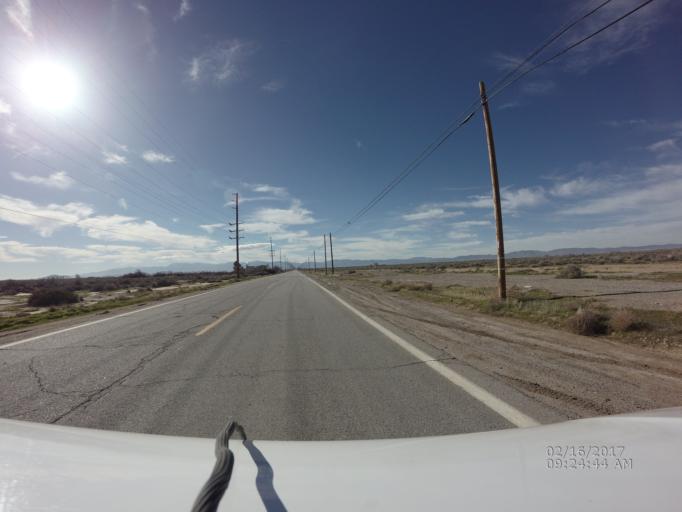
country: US
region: California
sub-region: Kern County
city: Edwards Air Force Base
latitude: 34.7628
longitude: -117.9699
